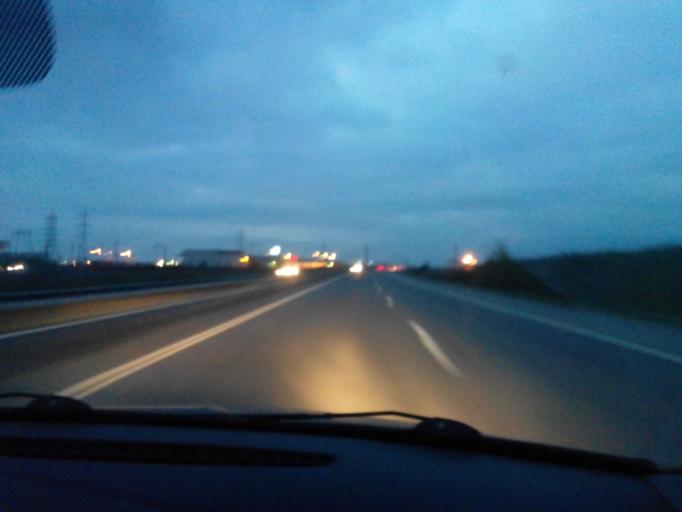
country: RO
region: Ilfov
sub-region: Comuna Dragomiresti-Vale
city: Dragomiresti-Deal
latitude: 44.4401
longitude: 25.9292
